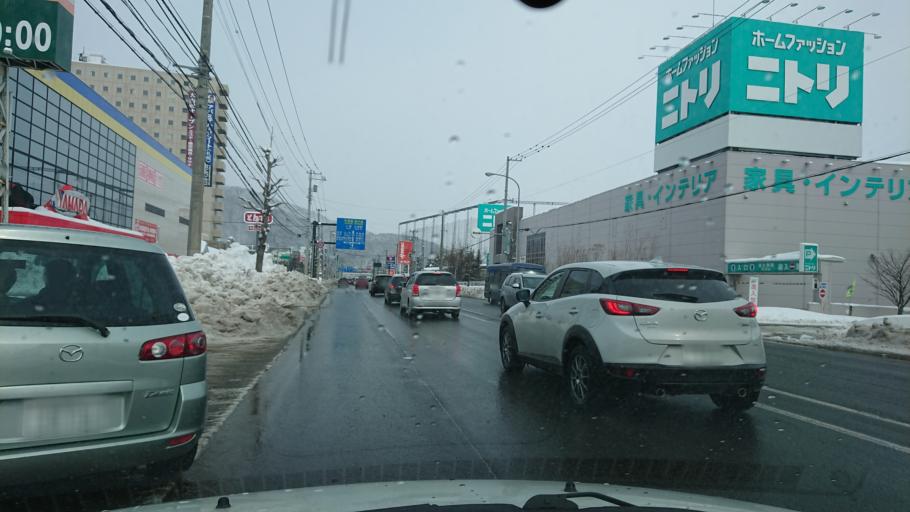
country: JP
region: Hokkaido
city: Sapporo
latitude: 42.9931
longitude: 141.3350
